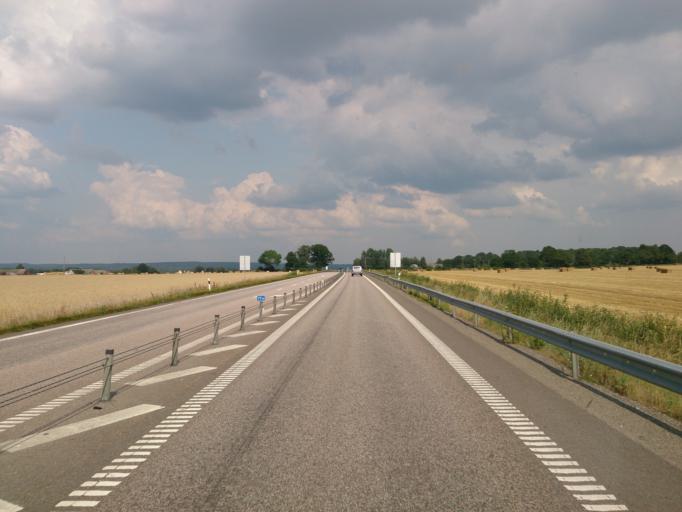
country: SE
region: Skane
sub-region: Hoors Kommun
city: Satofta
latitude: 55.8390
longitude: 13.5720
